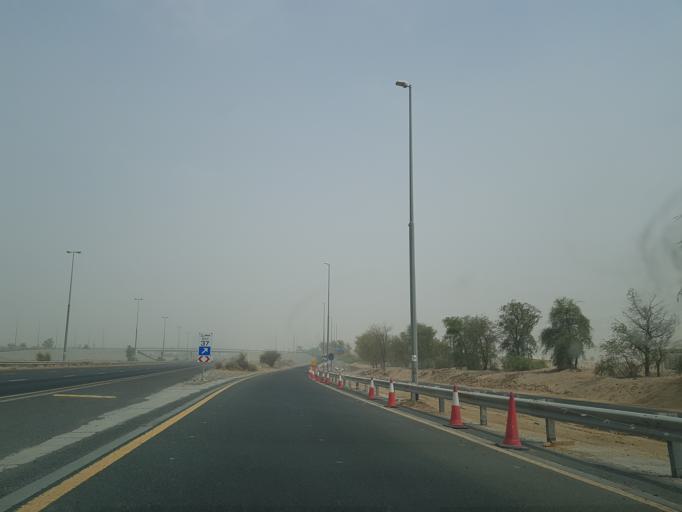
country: AE
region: Dubai
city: Dubai
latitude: 24.9499
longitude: 55.5049
